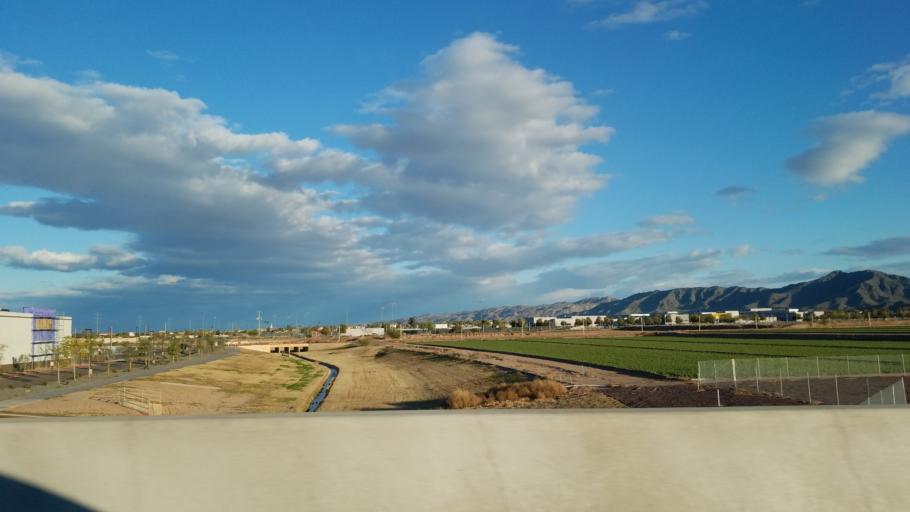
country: US
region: Arizona
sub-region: Maricopa County
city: Laveen
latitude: 33.3748
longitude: -112.1892
